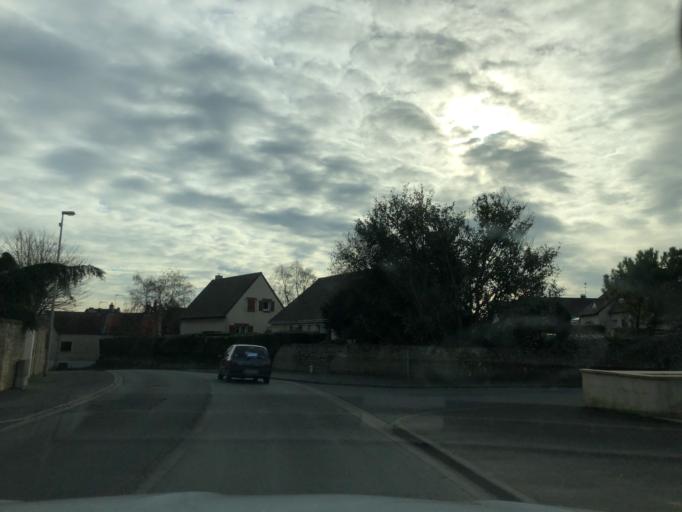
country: FR
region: Lower Normandy
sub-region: Departement du Calvados
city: Beuville
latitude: 49.2452
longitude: -0.3307
